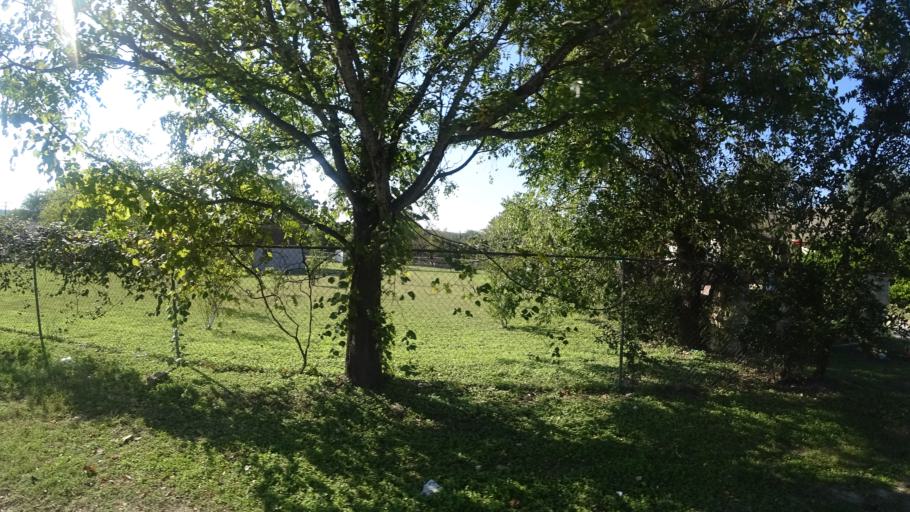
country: US
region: Texas
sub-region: Travis County
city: Austin
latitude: 30.3416
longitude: -97.6746
